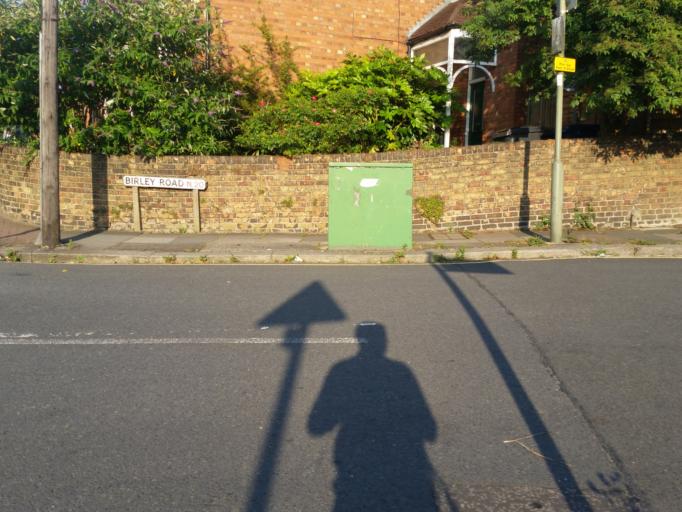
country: GB
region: England
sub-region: Greater London
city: Barnet
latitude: 51.6300
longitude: -0.1773
